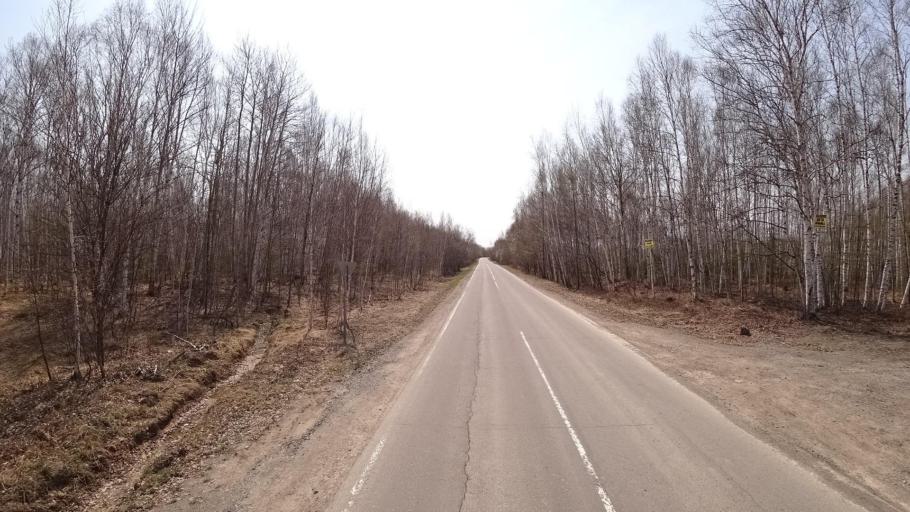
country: RU
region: Khabarovsk Krai
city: Selikhino
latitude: 50.3957
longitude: 137.3735
